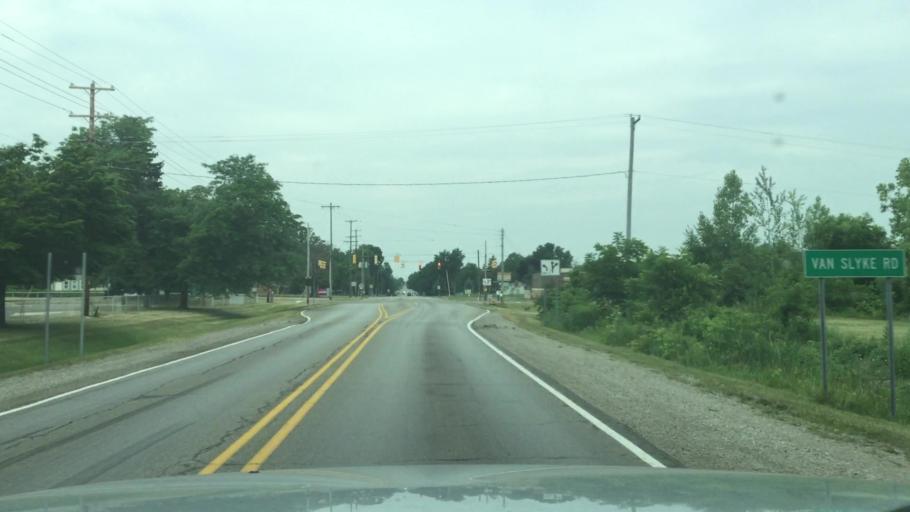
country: US
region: Michigan
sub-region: Genesee County
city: Flint
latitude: 42.9593
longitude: -83.7110
